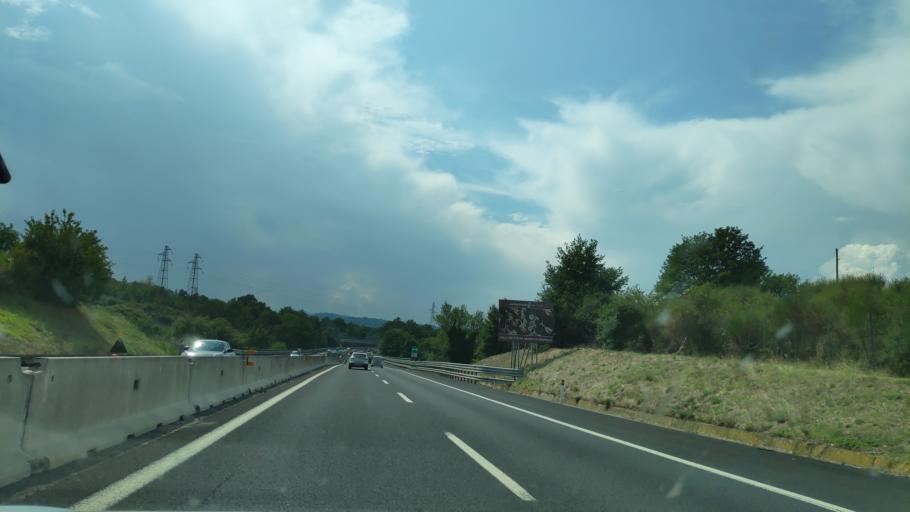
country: IT
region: Tuscany
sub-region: Province of Arezzo
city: Ponticino
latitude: 43.4840
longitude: 11.7165
